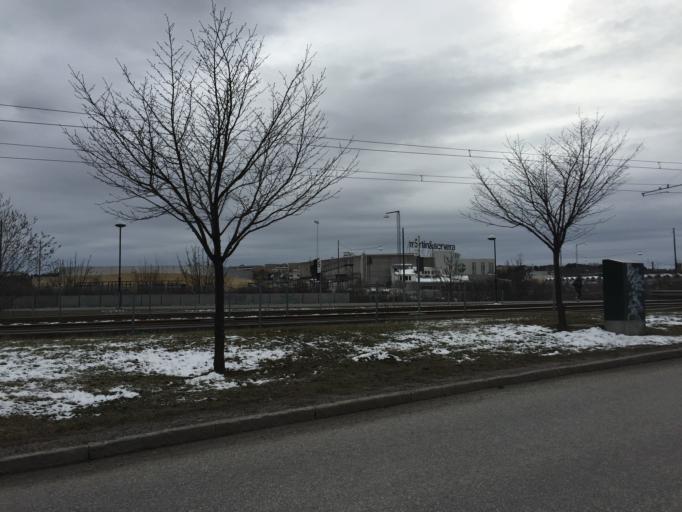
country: SE
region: Stockholm
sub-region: Stockholms Kommun
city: Arsta
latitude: 59.2965
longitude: 18.0388
